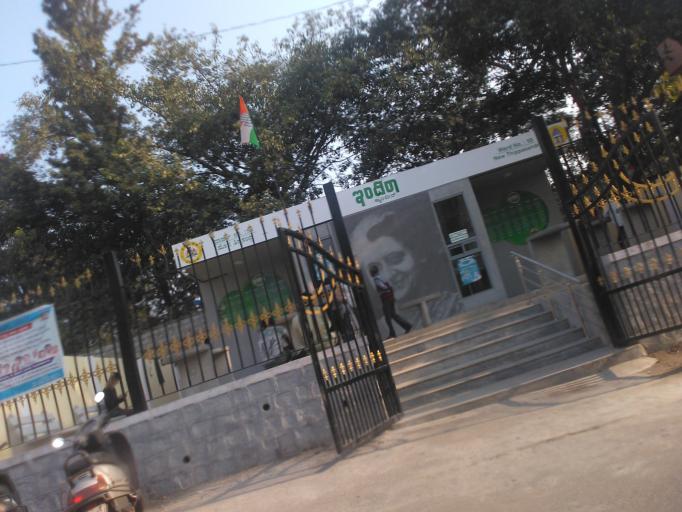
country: IN
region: Karnataka
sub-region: Bangalore Urban
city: Bangalore
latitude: 12.9745
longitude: 77.6487
